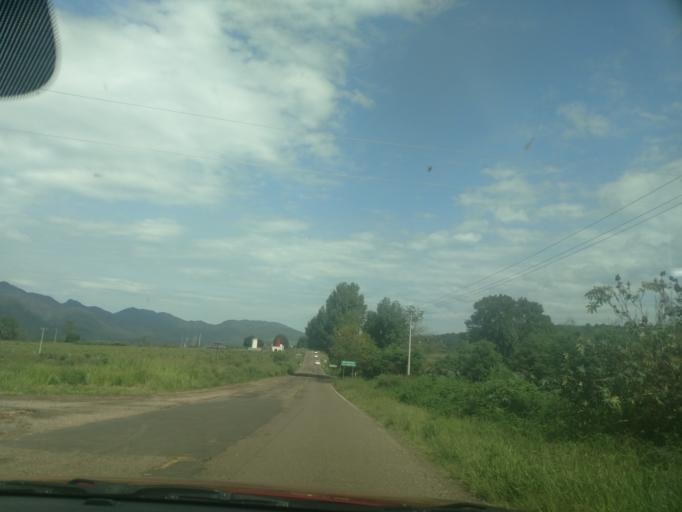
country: MX
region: Jalisco
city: Talpa de Allende
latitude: 20.4381
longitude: -104.7494
